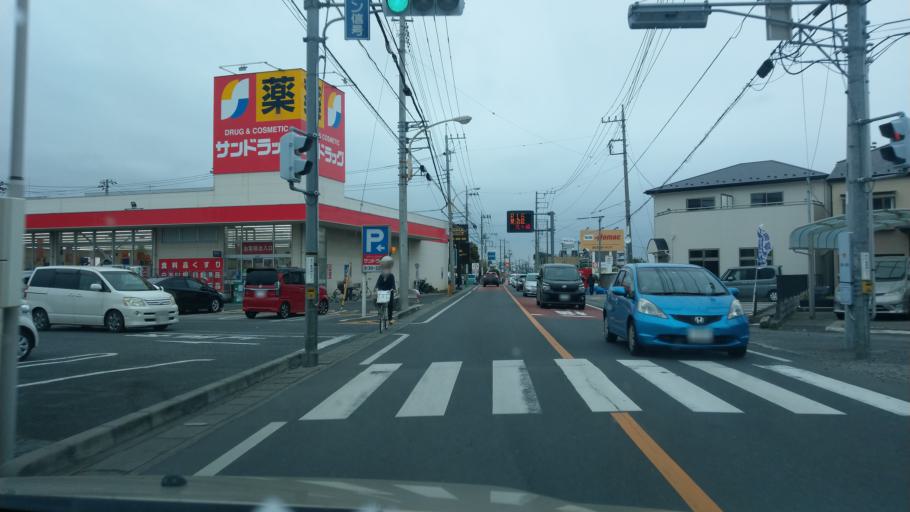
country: JP
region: Saitama
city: Saitama
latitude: 35.9287
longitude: 139.6631
